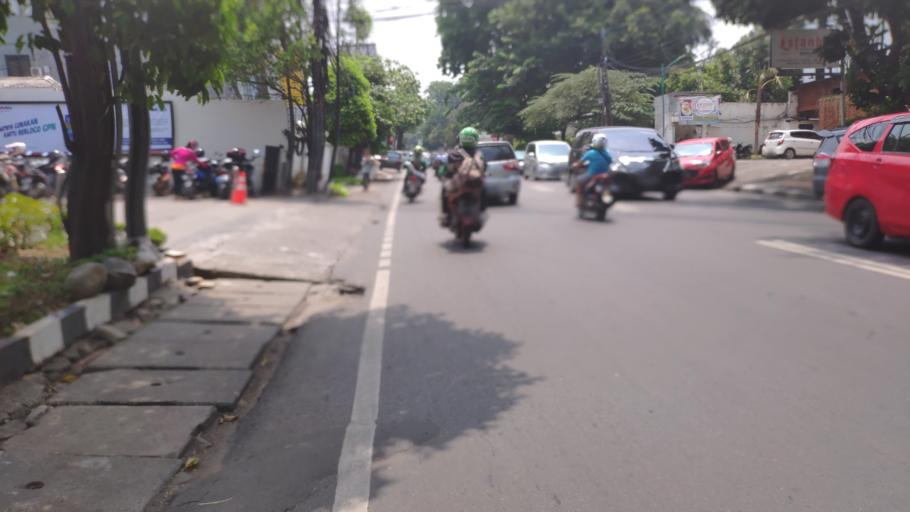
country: ID
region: Jakarta Raya
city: Jakarta
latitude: -6.2750
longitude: 106.8209
